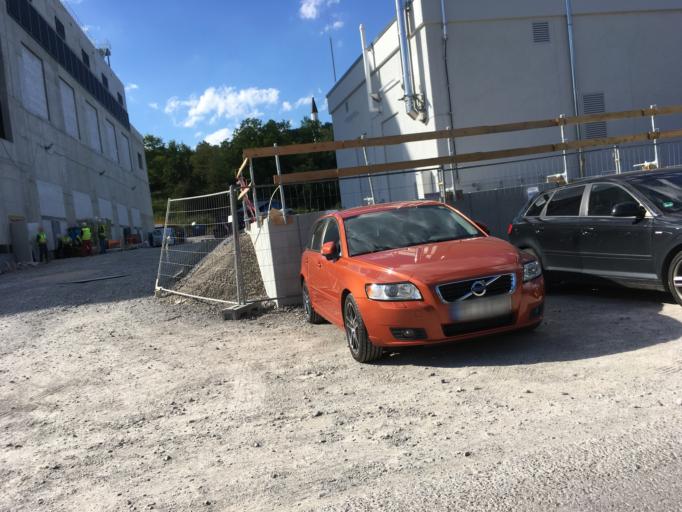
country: DE
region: Baden-Wuerttemberg
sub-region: Karlsruhe Region
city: Eutingen
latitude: 48.8977
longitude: 8.7274
